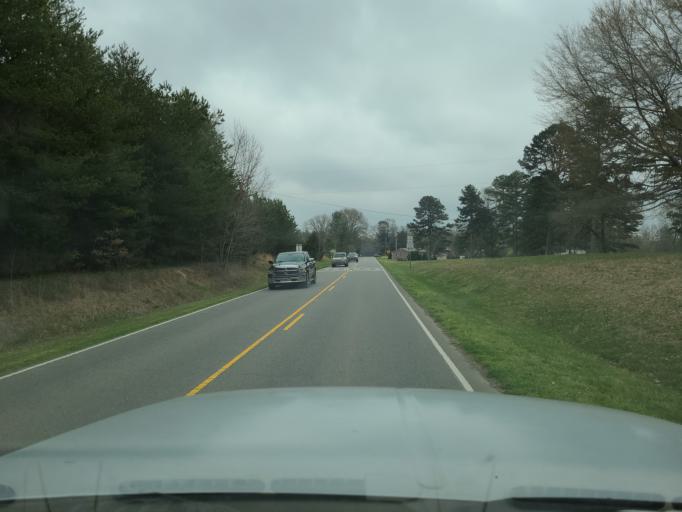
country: US
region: North Carolina
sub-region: Cleveland County
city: Shelby
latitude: 35.3850
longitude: -81.6212
